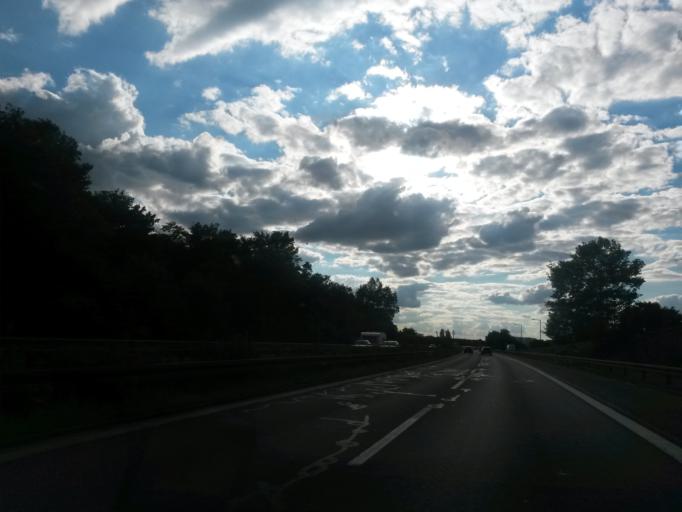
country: DE
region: Bavaria
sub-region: Regierungsbezirk Mittelfranken
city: Grossreuth bei Schweinau
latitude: 49.4316
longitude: 11.0180
